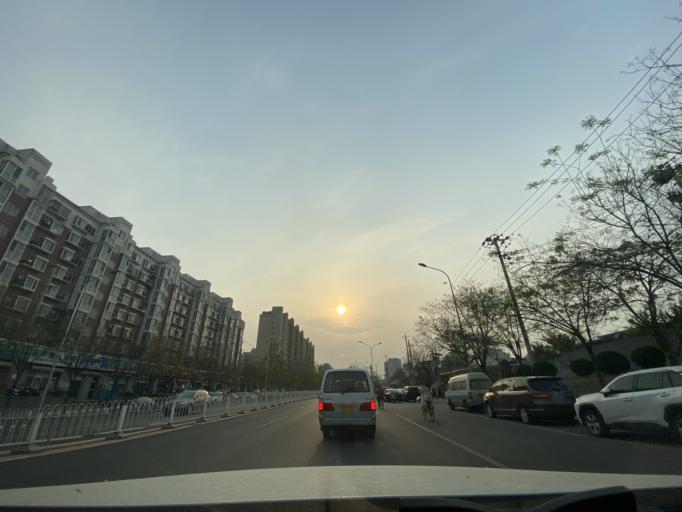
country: CN
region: Beijing
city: Babaoshan
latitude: 39.9283
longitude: 116.2417
